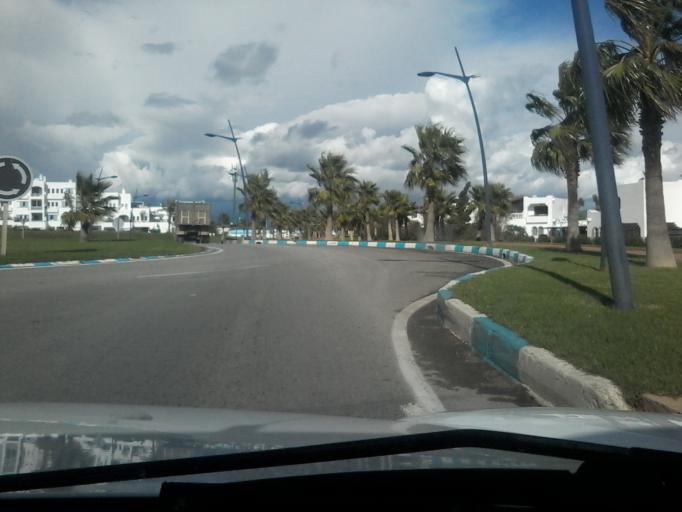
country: ES
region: Ceuta
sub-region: Ceuta
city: Ceuta
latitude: 35.7481
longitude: -5.3465
